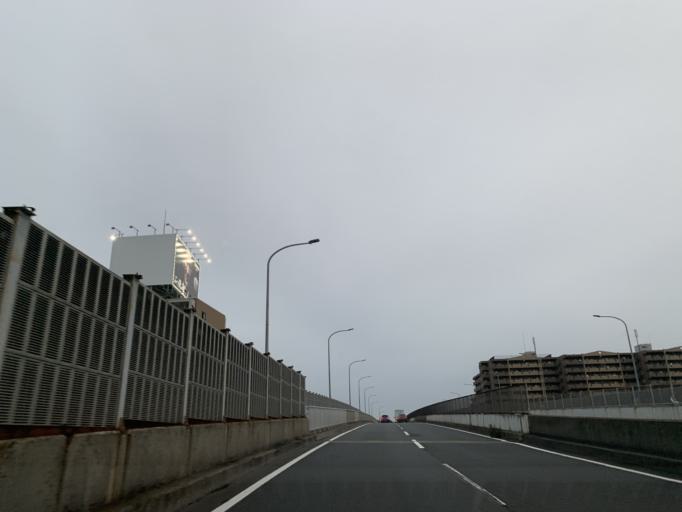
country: JP
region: Chiba
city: Funabashi
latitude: 35.6579
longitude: 140.0329
